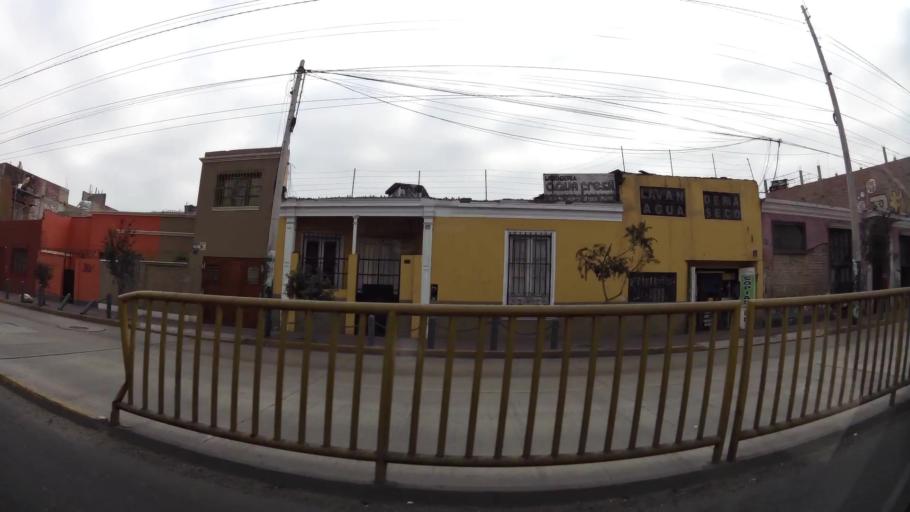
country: PE
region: Lima
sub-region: Lima
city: Surco
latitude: -12.1498
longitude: -77.0202
